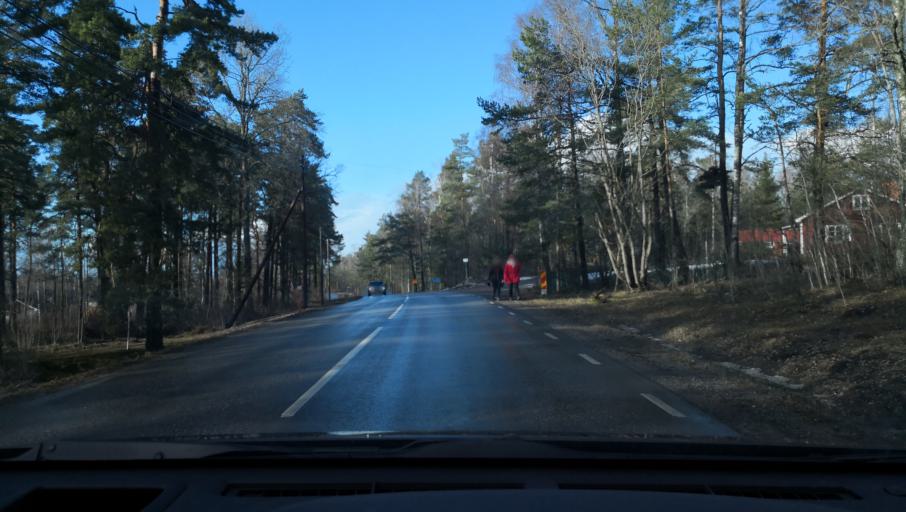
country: SE
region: Vaestmanland
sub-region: Arboga Kommun
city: Arboga
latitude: 59.3760
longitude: 15.8422
